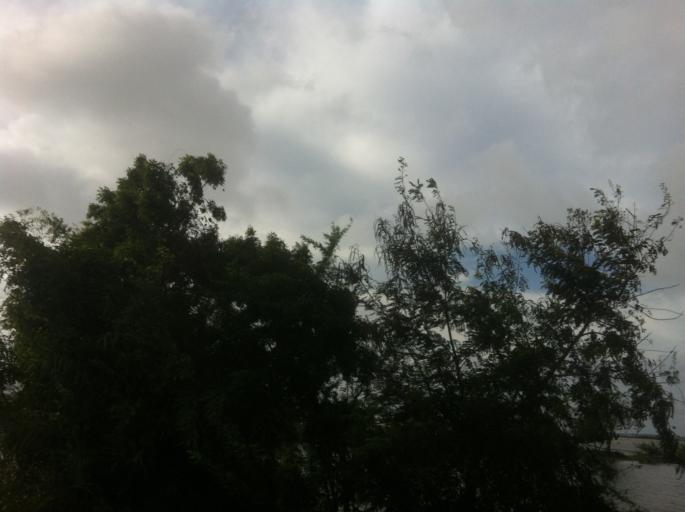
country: IN
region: Tamil Nadu
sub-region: Villupuram
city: Marakkanam
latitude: 12.2120
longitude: 79.9702
